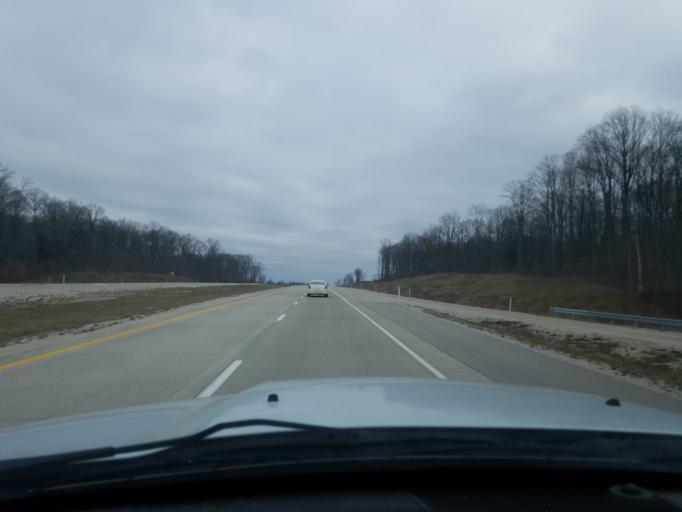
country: US
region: Indiana
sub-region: Greene County
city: Bloomfield
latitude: 38.9755
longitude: -86.7339
